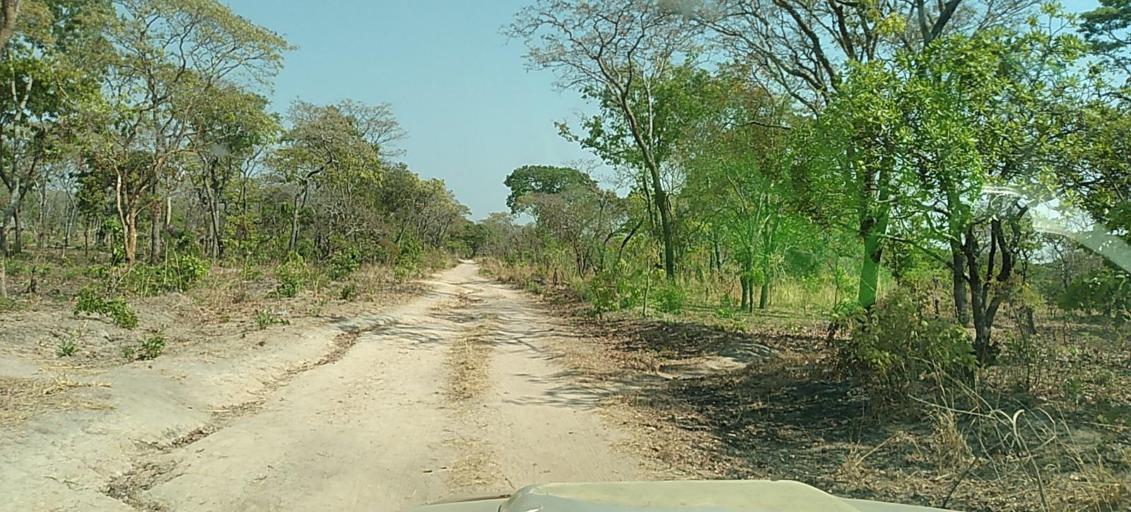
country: ZM
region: North-Western
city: Kalengwa
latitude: -13.3026
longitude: 24.7984
